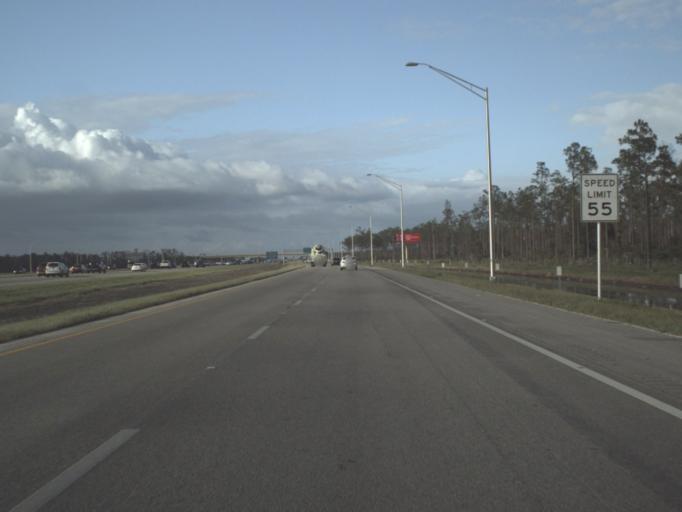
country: US
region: Florida
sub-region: Lee County
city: Three Oaks
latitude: 26.5014
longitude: -81.7940
